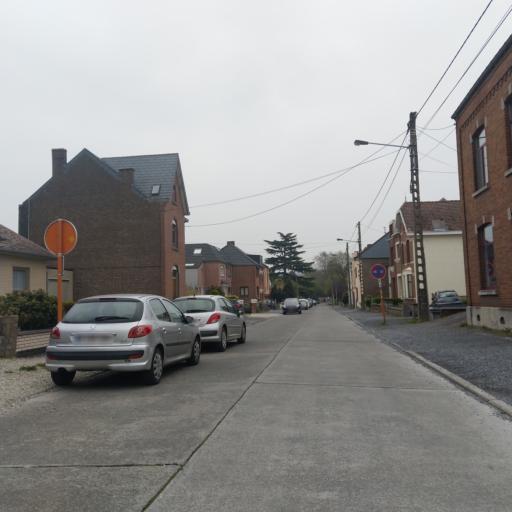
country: BE
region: Wallonia
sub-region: Province du Hainaut
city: Chasse Royale
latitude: 50.4401
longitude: 3.9520
